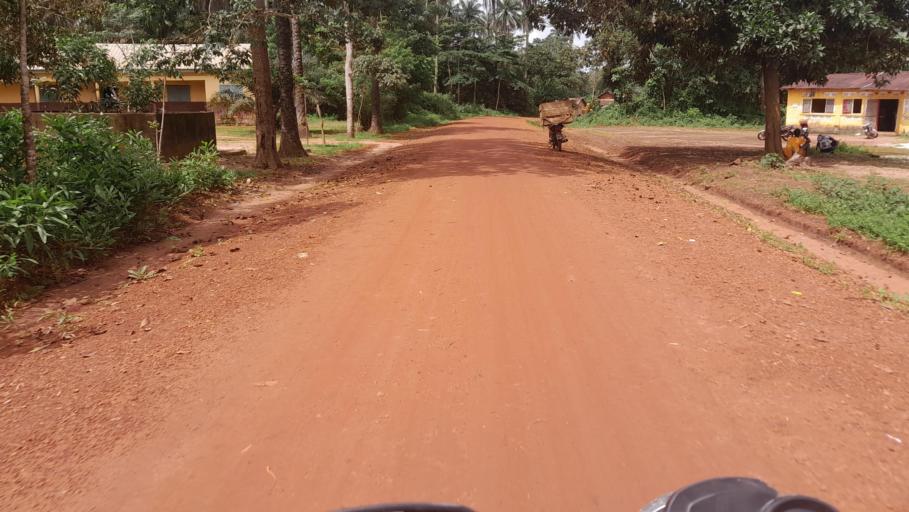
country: GN
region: Boke
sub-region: Boffa
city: Boffa
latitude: 10.0279
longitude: -13.8822
